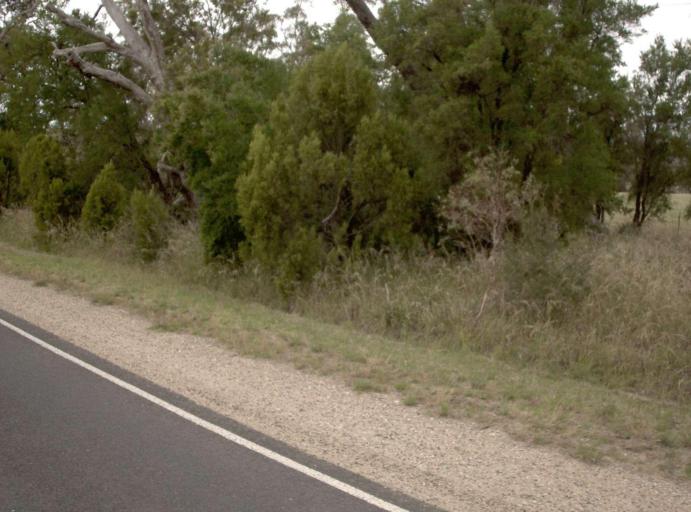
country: AU
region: Victoria
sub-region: Wellington
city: Sale
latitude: -38.1760
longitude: 147.1219
